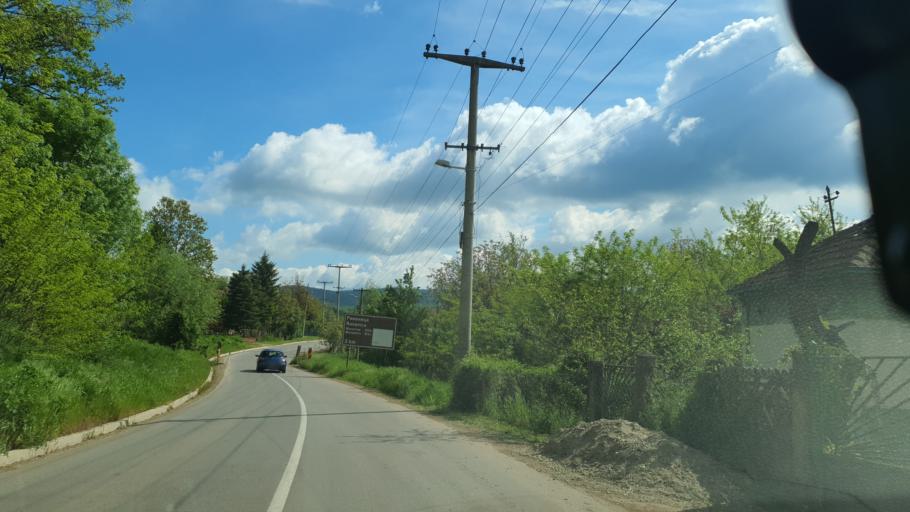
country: RS
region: Central Serbia
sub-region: Pomoravski Okrug
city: Cuprija
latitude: 43.9579
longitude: 21.4699
